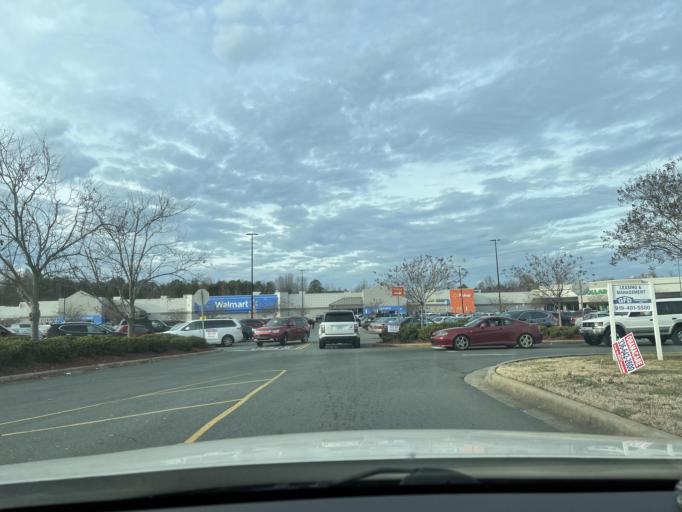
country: US
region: North Carolina
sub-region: Alamance County
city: Elon
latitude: 36.0706
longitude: -79.4979
